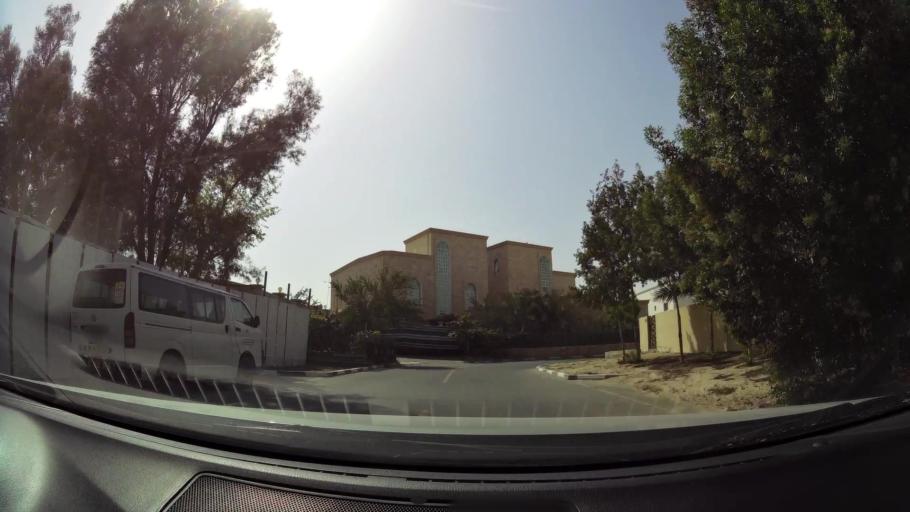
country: AE
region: Dubai
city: Dubai
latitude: 25.1633
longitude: 55.2511
